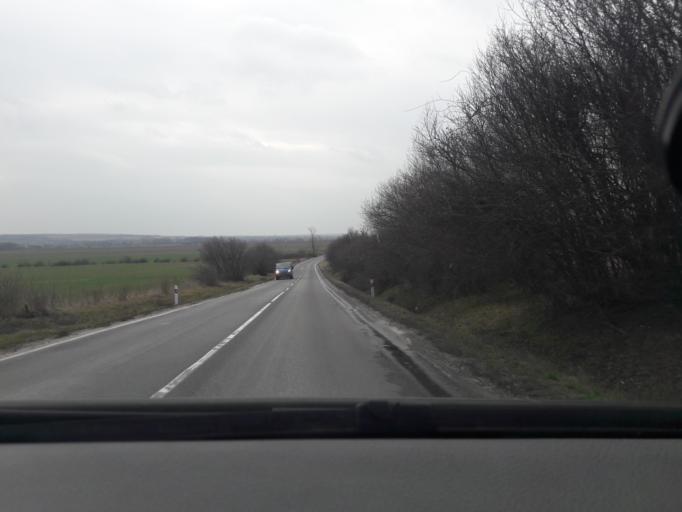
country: SK
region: Trnavsky
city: Smolenice
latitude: 48.4310
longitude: 17.4210
